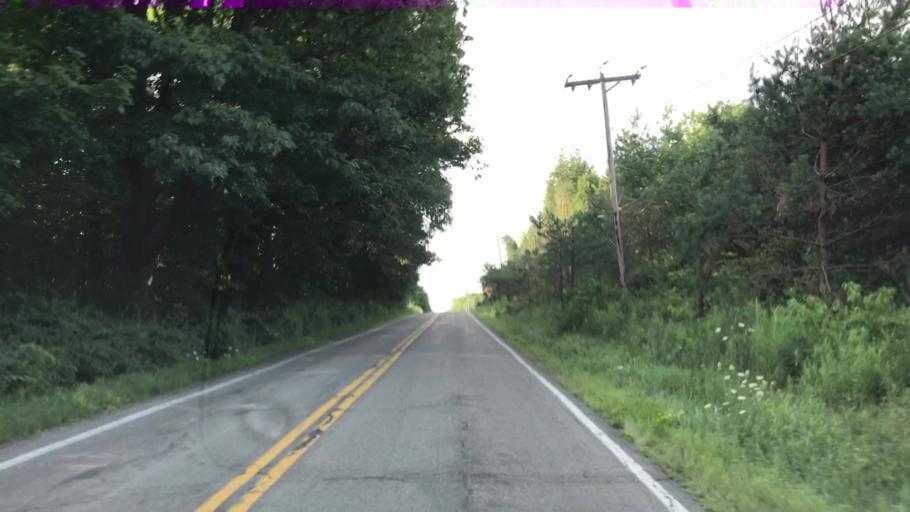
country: US
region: New York
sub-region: Chautauqua County
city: Mayville
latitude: 42.2611
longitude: -79.4698
